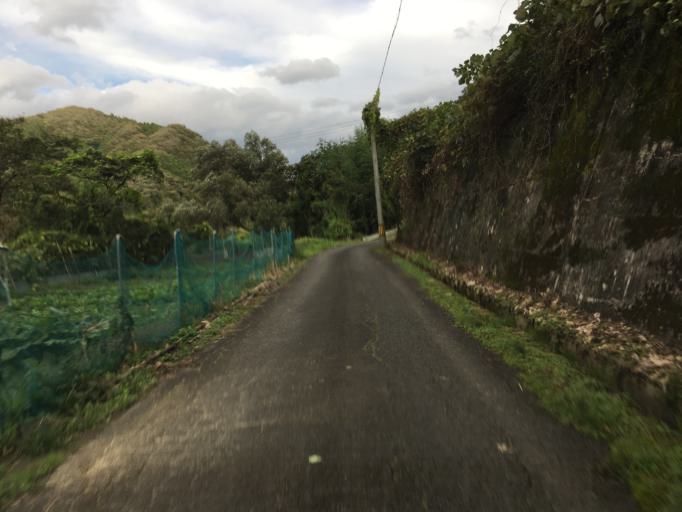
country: JP
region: Miyagi
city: Marumori
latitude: 37.9334
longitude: 140.7127
